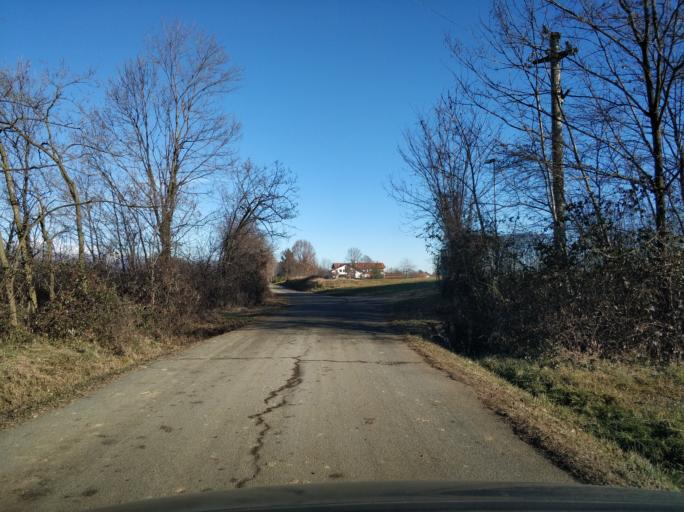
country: IT
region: Piedmont
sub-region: Provincia di Torino
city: San Francesco al Campo
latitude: 45.2360
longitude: 7.6422
